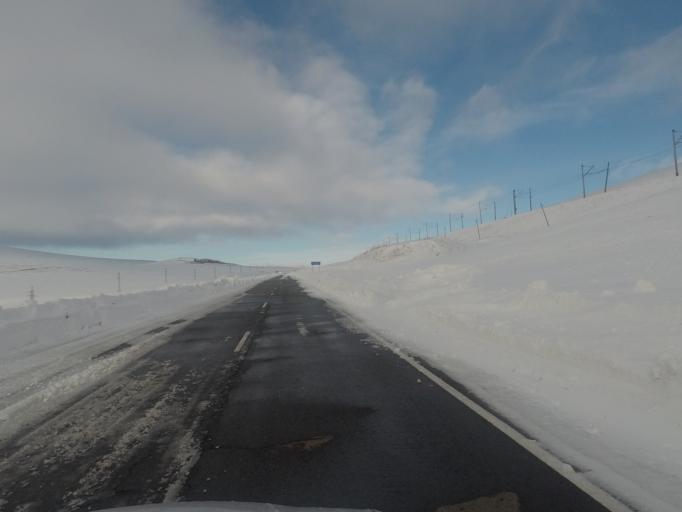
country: GE
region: Kvemo Kartli
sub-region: Tsalka
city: Tsalka
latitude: 41.4820
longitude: 43.8527
